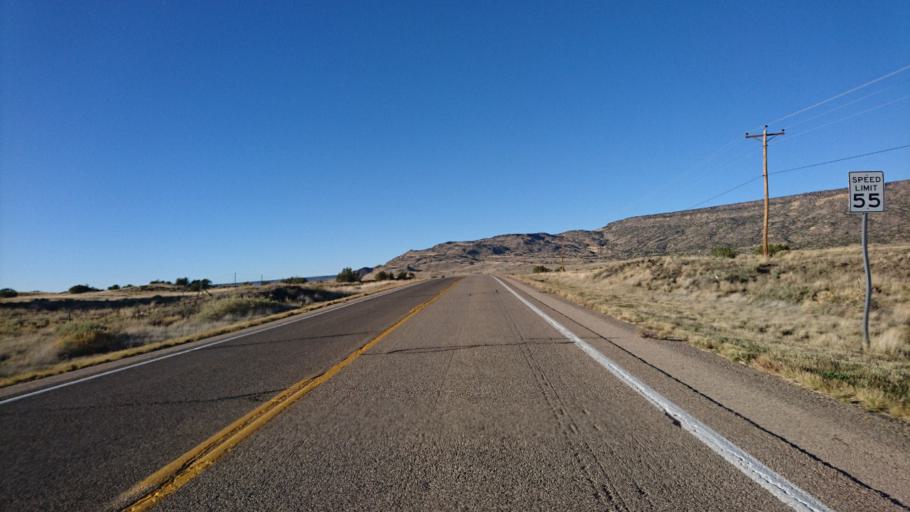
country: US
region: New Mexico
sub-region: Cibola County
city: Grants
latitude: 35.0903
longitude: -107.7705
